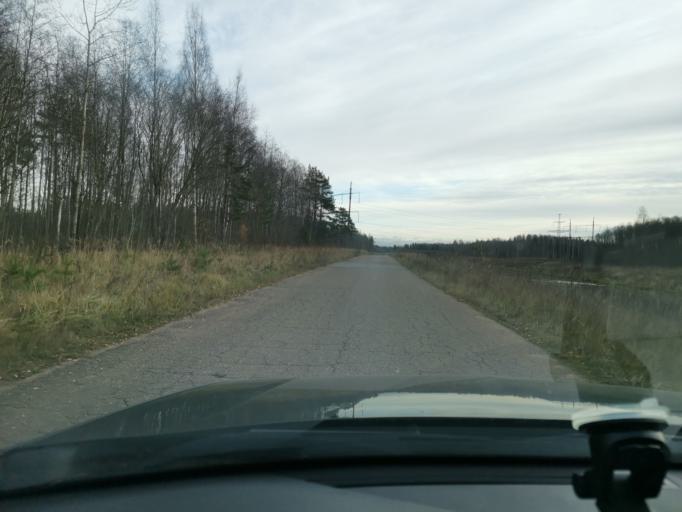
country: EE
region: Ida-Virumaa
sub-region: Sillamaee linn
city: Sillamae
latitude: 59.2645
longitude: 27.9010
